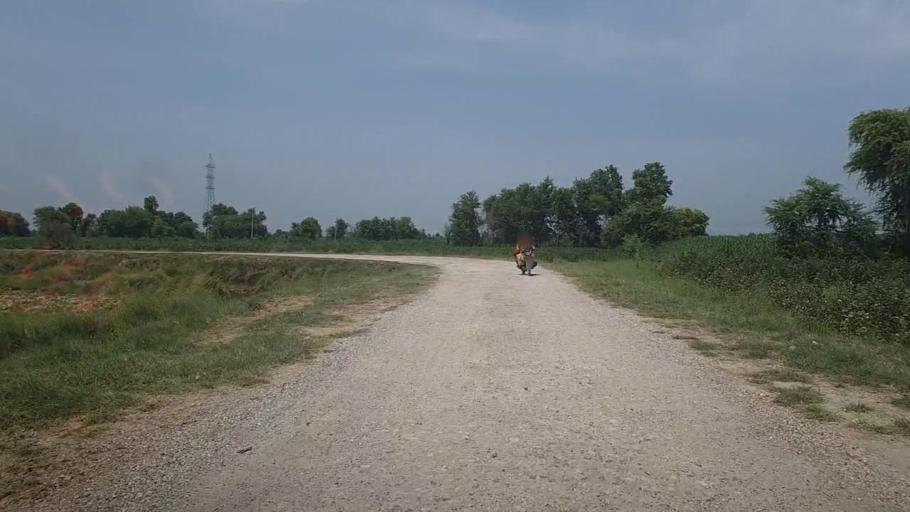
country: PK
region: Sindh
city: Ubauro
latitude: 28.1749
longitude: 69.7689
